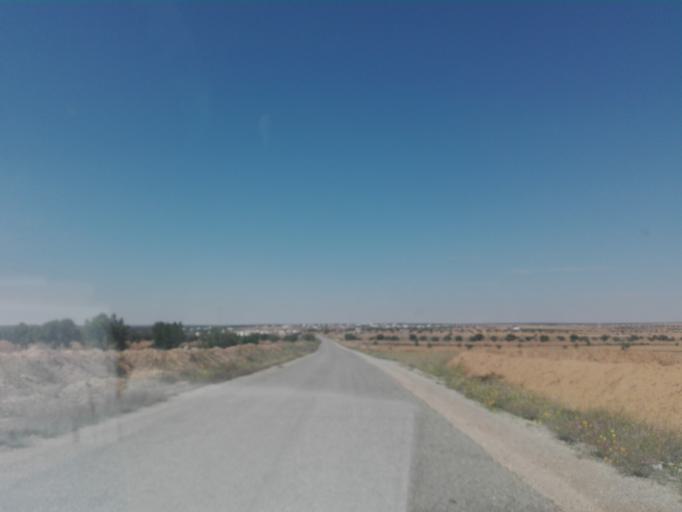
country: TN
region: Safaqis
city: Bi'r `Ali Bin Khalifah
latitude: 34.6730
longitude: 10.3771
